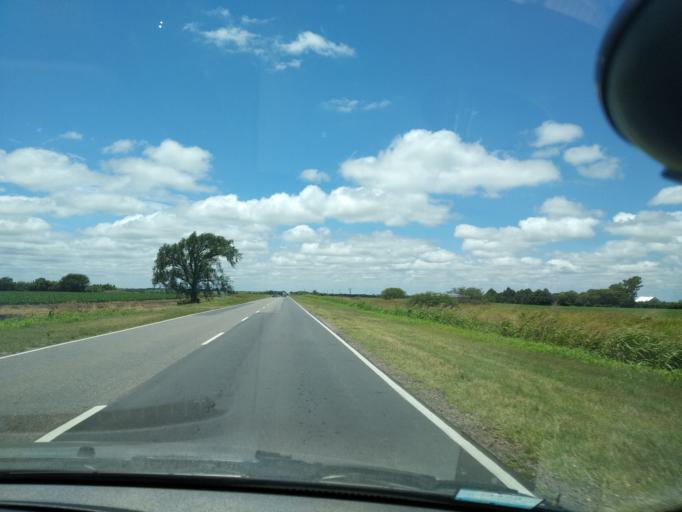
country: AR
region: Cordoba
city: Despenaderos
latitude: -31.6511
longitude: -64.1842
